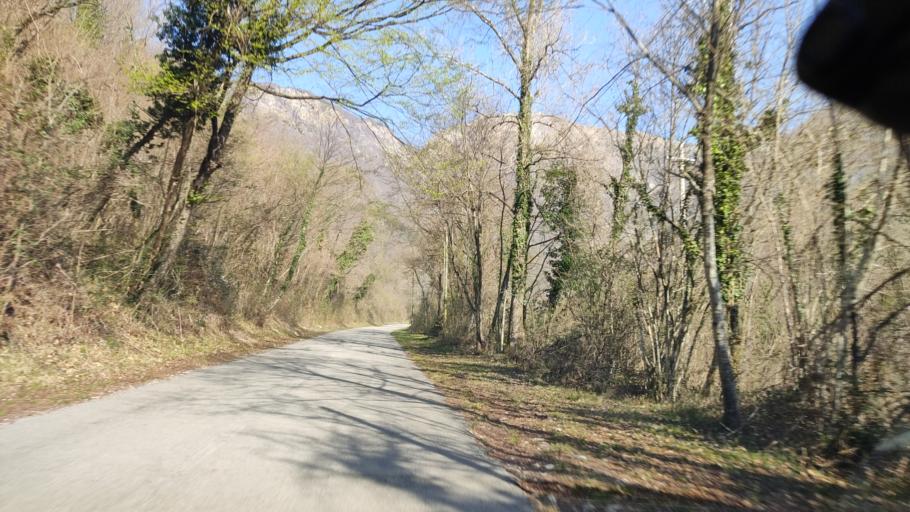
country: IT
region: Friuli Venezia Giulia
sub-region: Provincia di Pordenone
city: Budoia
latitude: 46.0636
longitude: 12.5157
